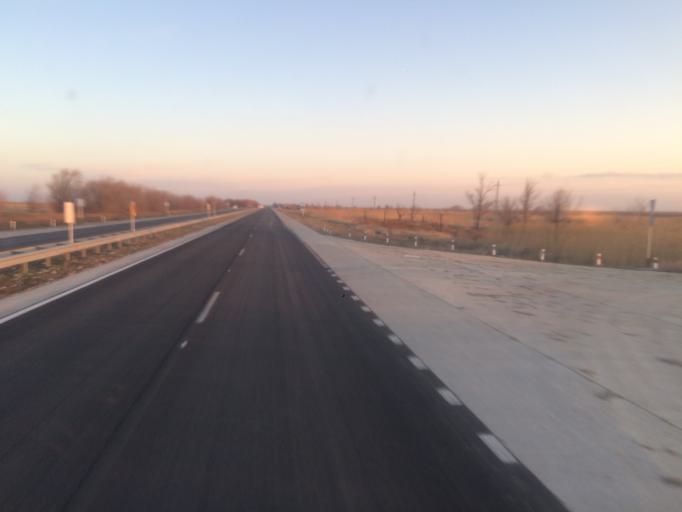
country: KZ
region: Ongtustik Qazaqstan
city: Bayaldyr
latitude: 43.0943
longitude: 68.6351
